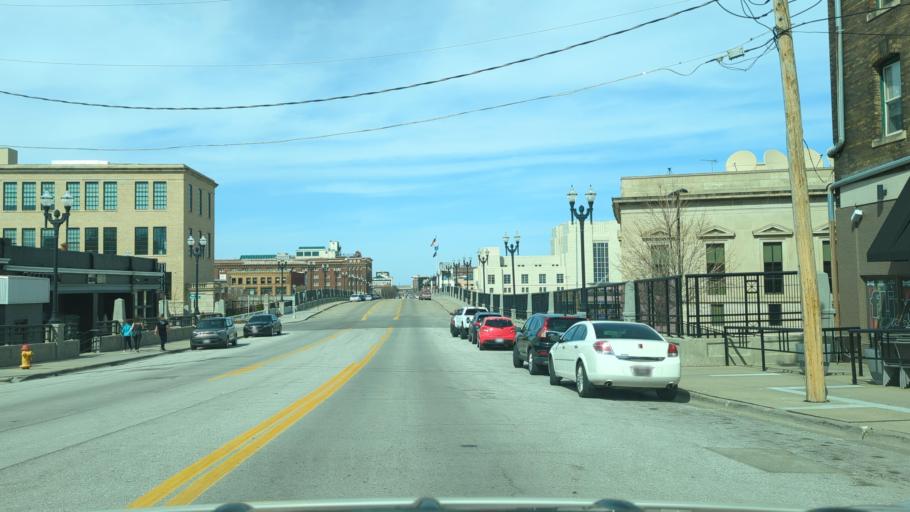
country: US
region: Nebraska
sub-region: Douglas County
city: Omaha
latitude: 41.2494
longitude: -95.9293
